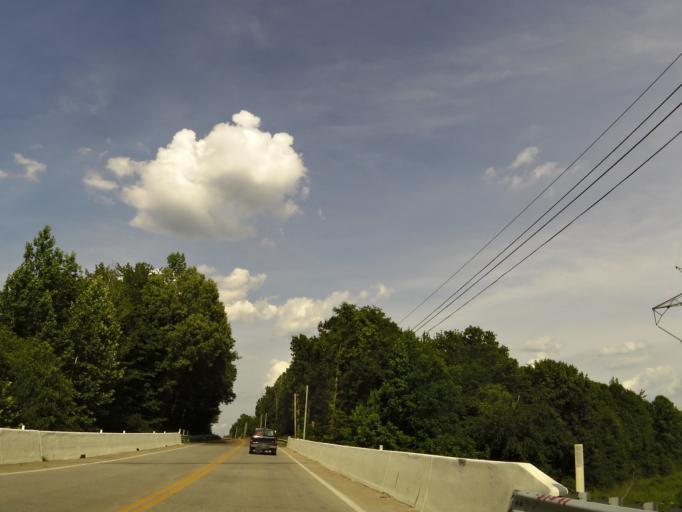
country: US
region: Tennessee
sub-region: Carroll County
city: Bruceton
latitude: 36.0343
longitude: -88.2060
